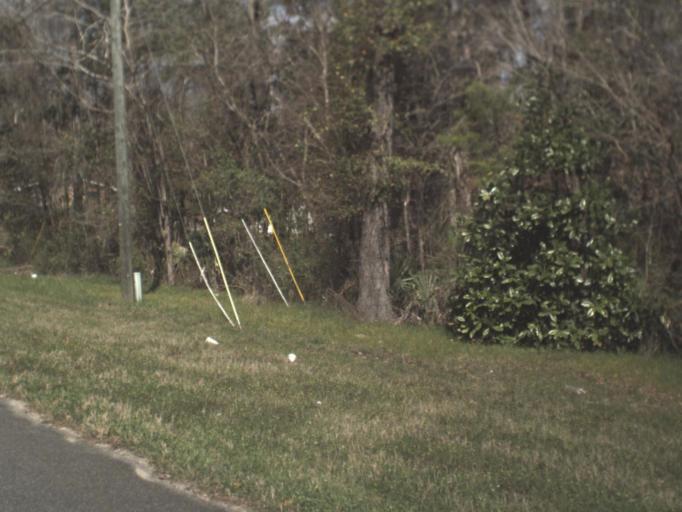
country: US
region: Florida
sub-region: Gadsden County
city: Quincy
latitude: 30.5950
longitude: -84.5315
